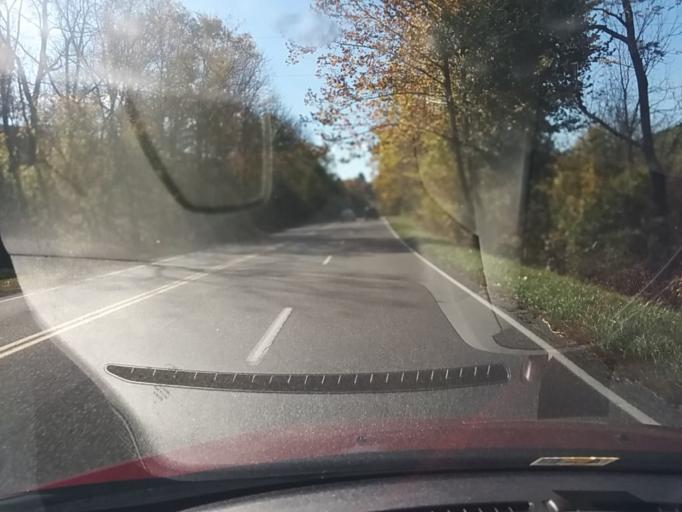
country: US
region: Virginia
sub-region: City of Lexington
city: Lexington
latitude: 37.7638
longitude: -79.4468
